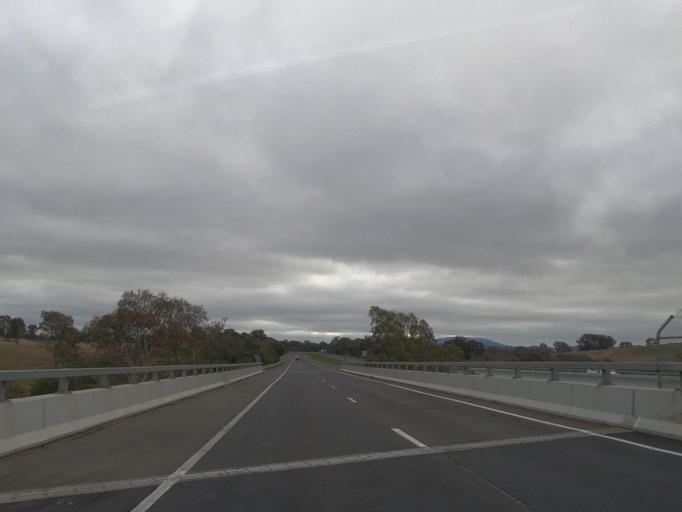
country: AU
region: Victoria
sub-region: Mount Alexander
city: Castlemaine
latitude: -37.1080
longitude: 144.3754
